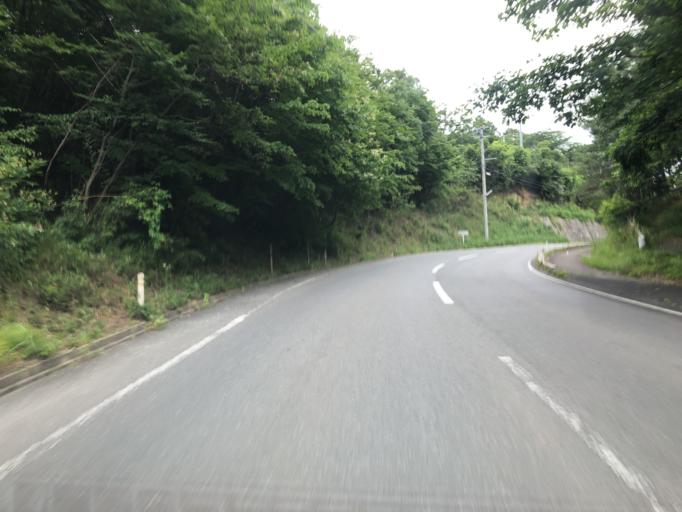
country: JP
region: Miyagi
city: Marumori
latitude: 37.8650
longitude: 140.8912
